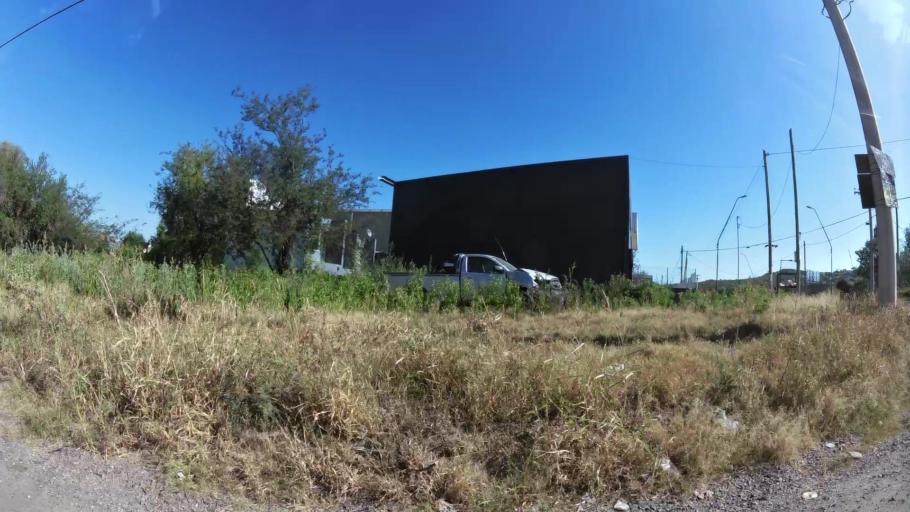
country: AR
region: Cordoba
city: La Calera
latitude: -31.3574
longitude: -64.3142
